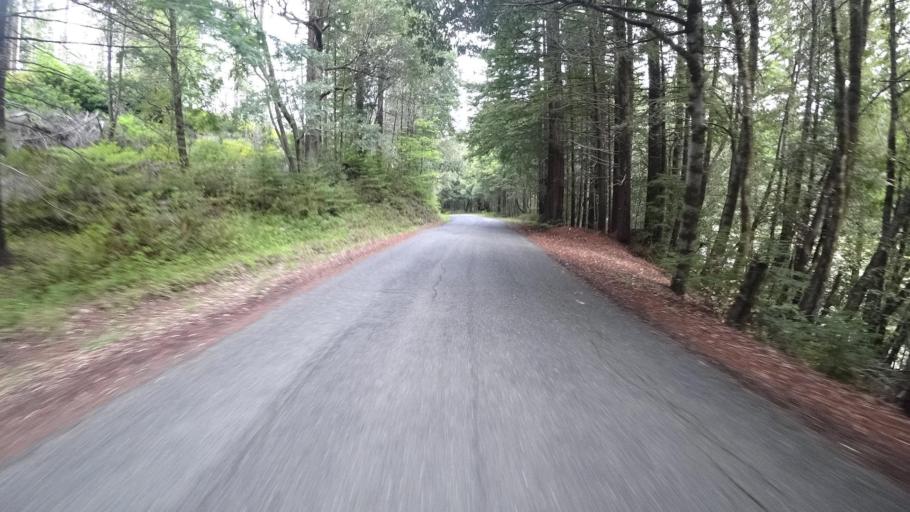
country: US
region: California
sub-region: Humboldt County
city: Redway
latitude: 40.3327
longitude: -123.8455
